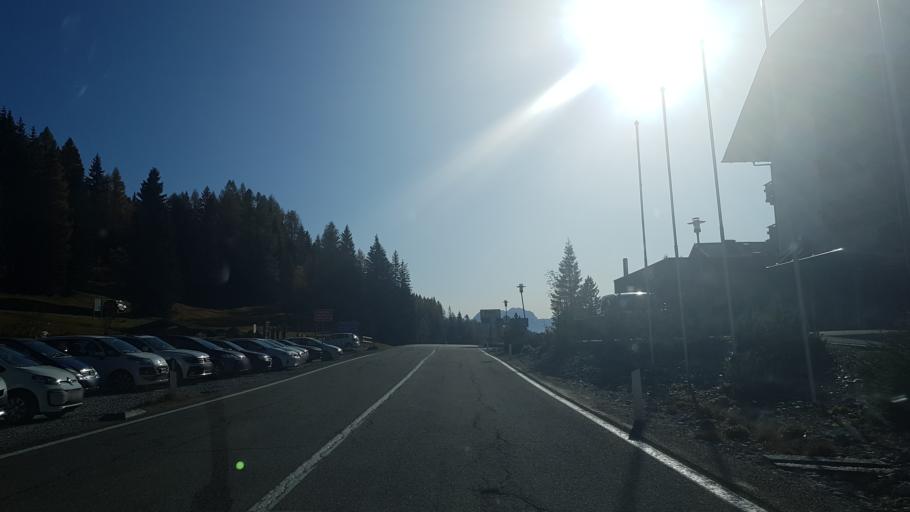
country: IT
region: Trentino-Alto Adige
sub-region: Bolzano
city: Sesto
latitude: 46.6562
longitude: 12.4196
